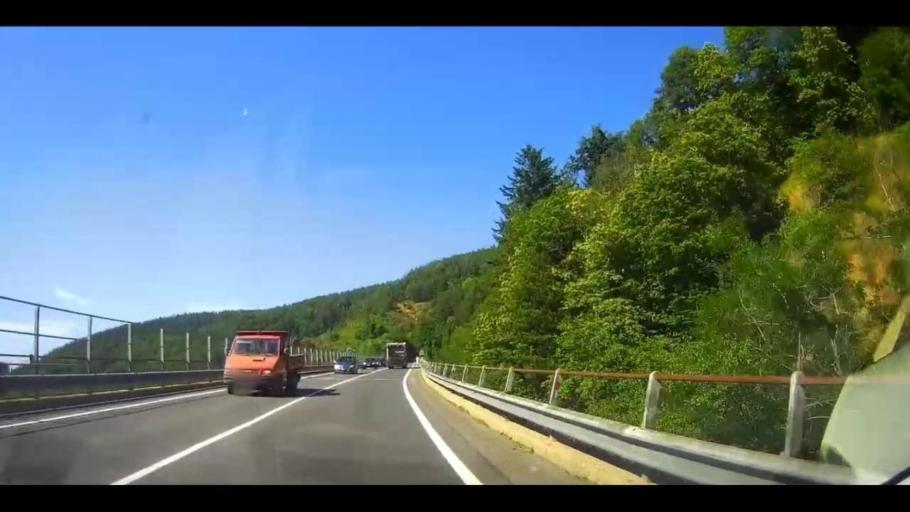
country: IT
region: Calabria
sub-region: Provincia di Cosenza
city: Celico
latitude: 39.3323
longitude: 16.3611
